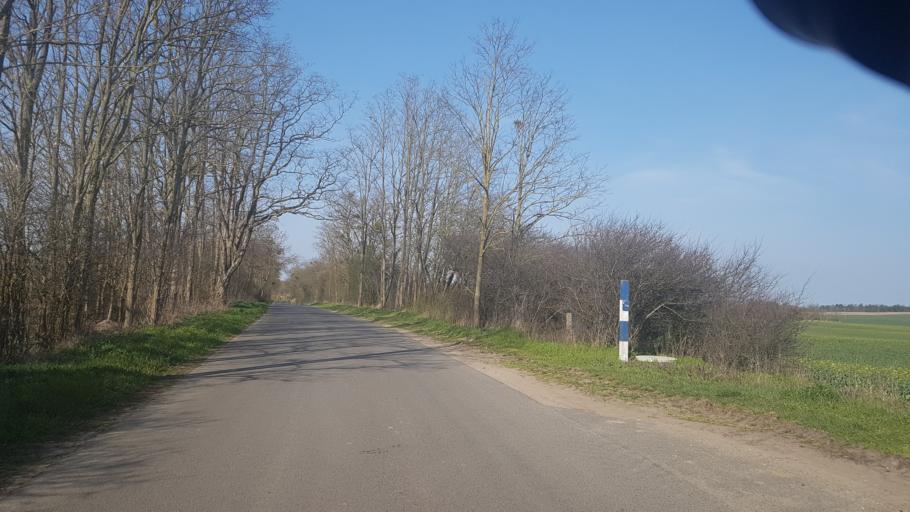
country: DE
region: Brandenburg
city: Gerswalde
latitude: 53.1924
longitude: 13.7805
